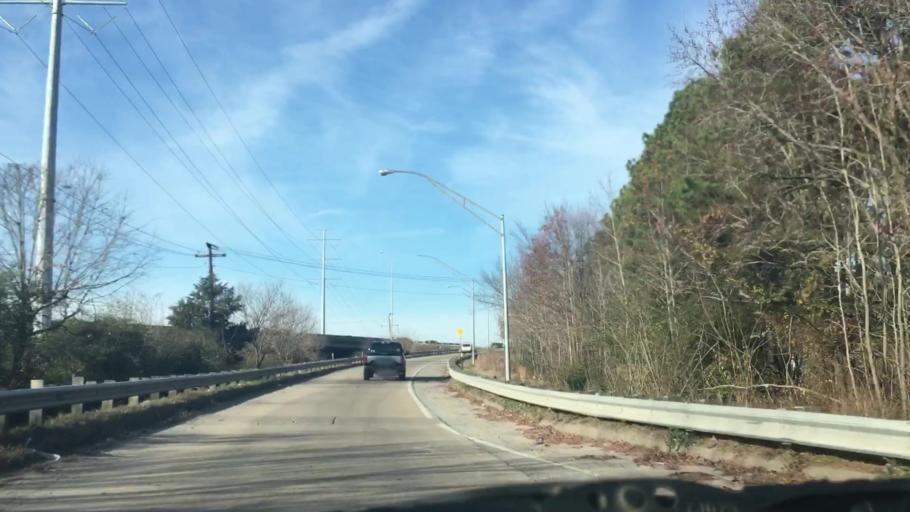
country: US
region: Virginia
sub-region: City of Chesapeake
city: Chesapeake
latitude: 36.8407
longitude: -76.1607
